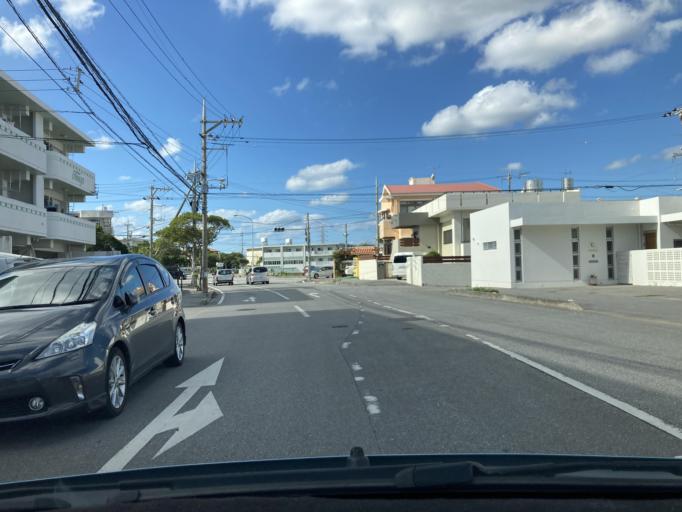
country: JP
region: Okinawa
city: Gushikawa
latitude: 26.3647
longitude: 127.8459
